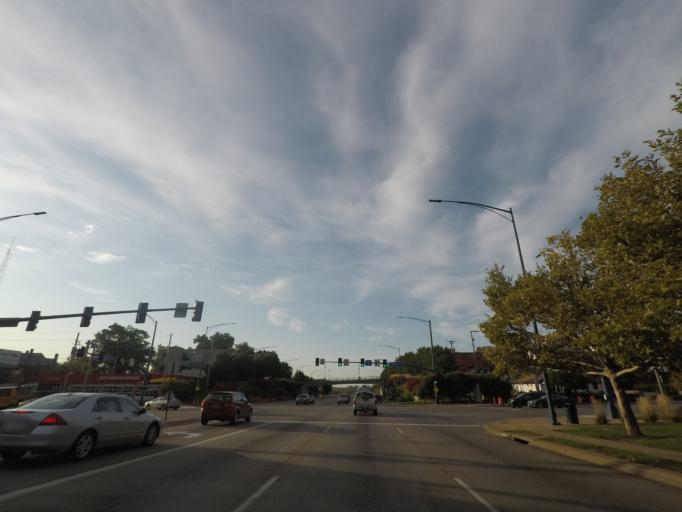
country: US
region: Iowa
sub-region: Polk County
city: Des Moines
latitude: 41.5861
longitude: -93.6449
